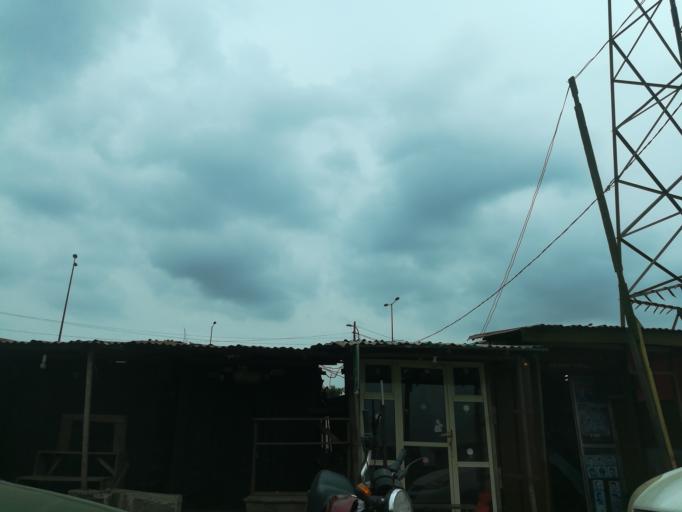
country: NG
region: Lagos
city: Ojota
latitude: 6.6111
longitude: 3.4136
